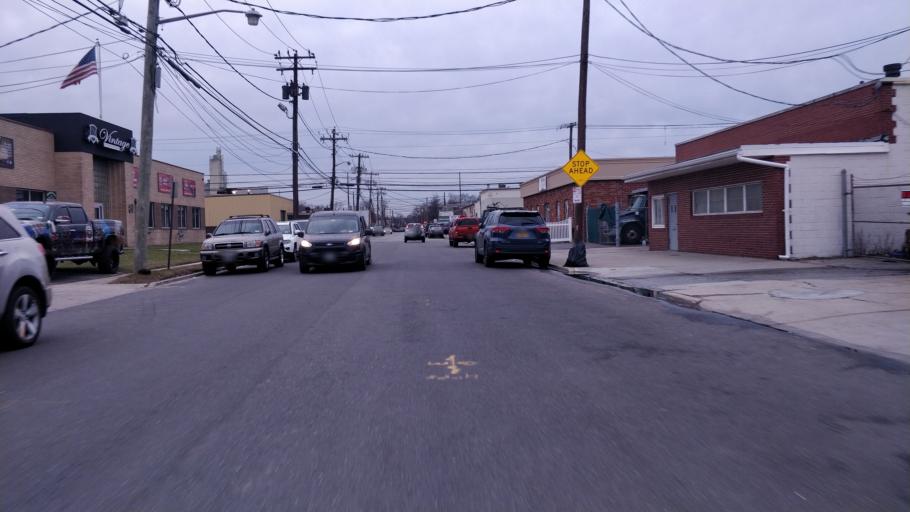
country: US
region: New York
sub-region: Nassau County
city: New Cassel
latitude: 40.7562
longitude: -73.5631
